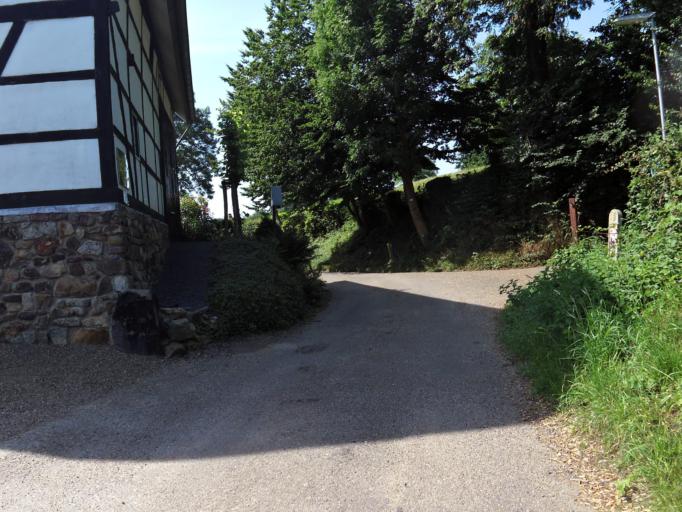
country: BE
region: Wallonia
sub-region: Province de Liege
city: Plombieres
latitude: 50.7730
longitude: 5.9169
